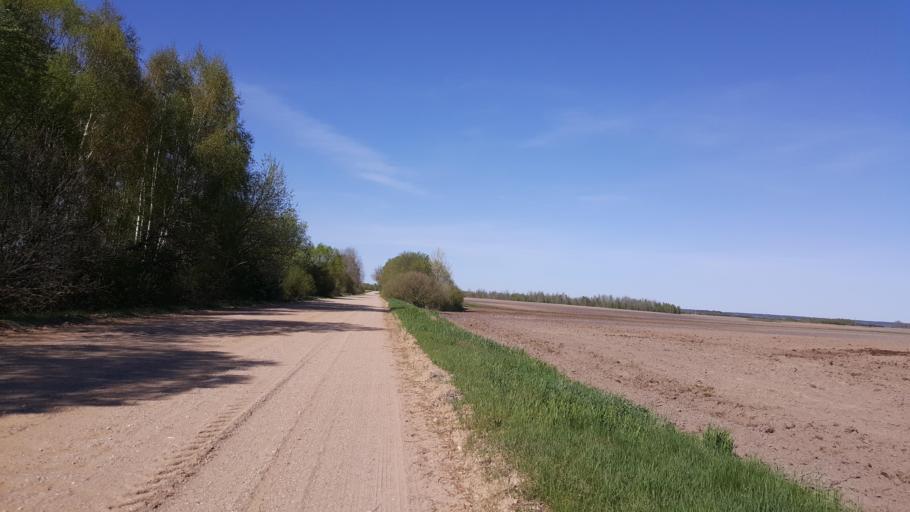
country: BY
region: Brest
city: Kamyanyets
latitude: 52.4266
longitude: 23.8805
